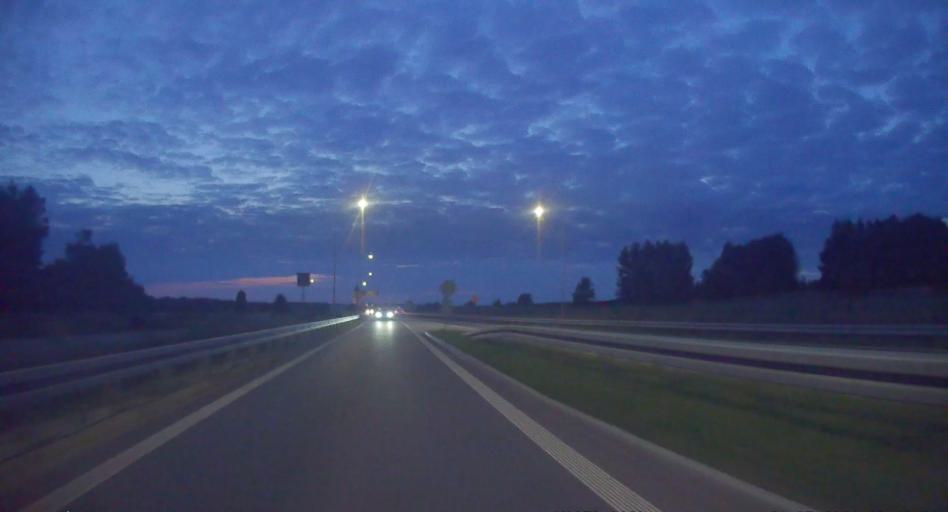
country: PL
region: Silesian Voivodeship
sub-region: Powiat klobucki
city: Kamyk
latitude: 50.8546
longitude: 19.0333
